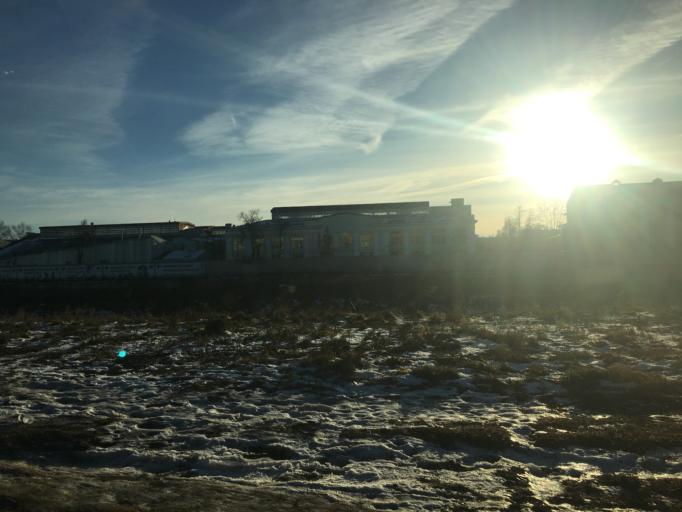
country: RU
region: Tula
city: Tula
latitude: 54.2051
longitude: 37.6104
